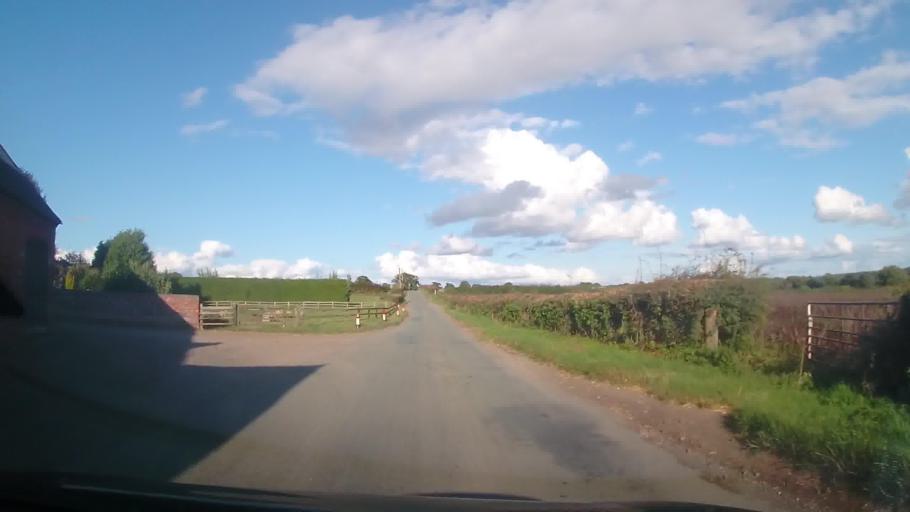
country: GB
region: England
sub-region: Shropshire
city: Bayston Hill
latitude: 52.6508
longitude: -2.7851
